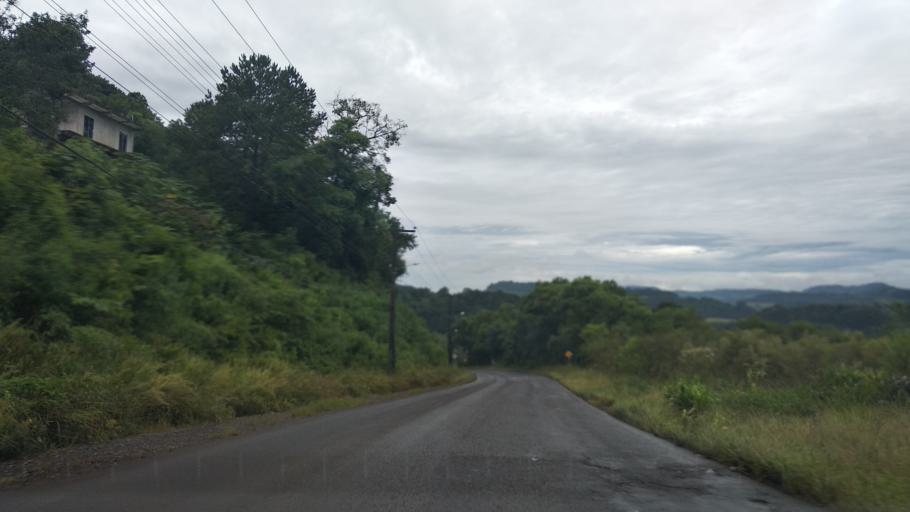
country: BR
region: Santa Catarina
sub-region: Videira
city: Videira
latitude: -26.9993
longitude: -51.1772
